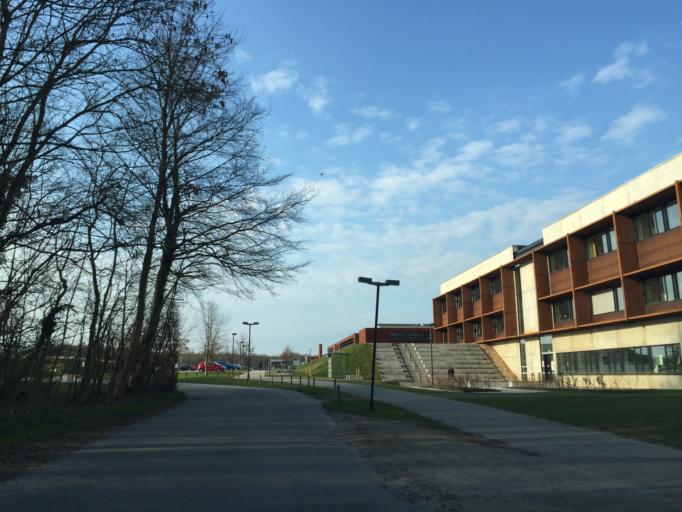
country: DK
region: South Denmark
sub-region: Odense Kommune
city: Neder Holluf
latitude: 55.3666
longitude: 10.4255
